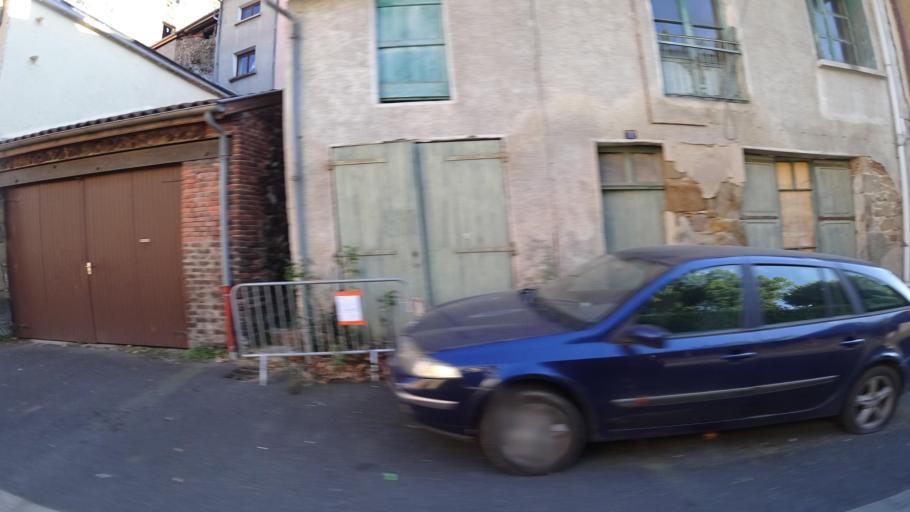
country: FR
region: Midi-Pyrenees
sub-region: Departement de l'Aveyron
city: Cransac
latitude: 44.5250
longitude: 2.2843
